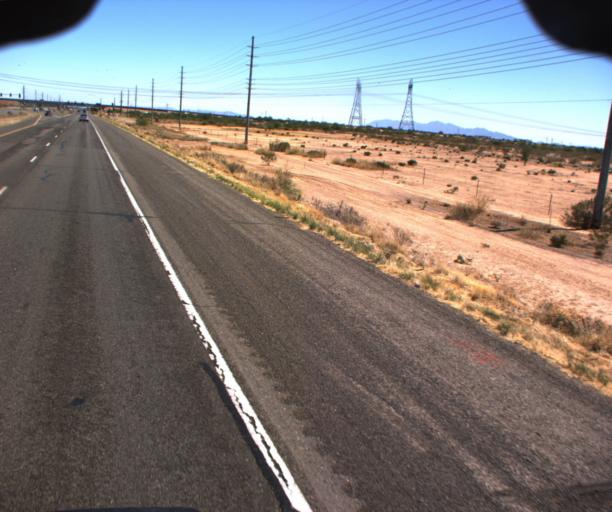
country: US
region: Arizona
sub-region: Maricopa County
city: Sun City West
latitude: 33.6887
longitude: -112.4146
